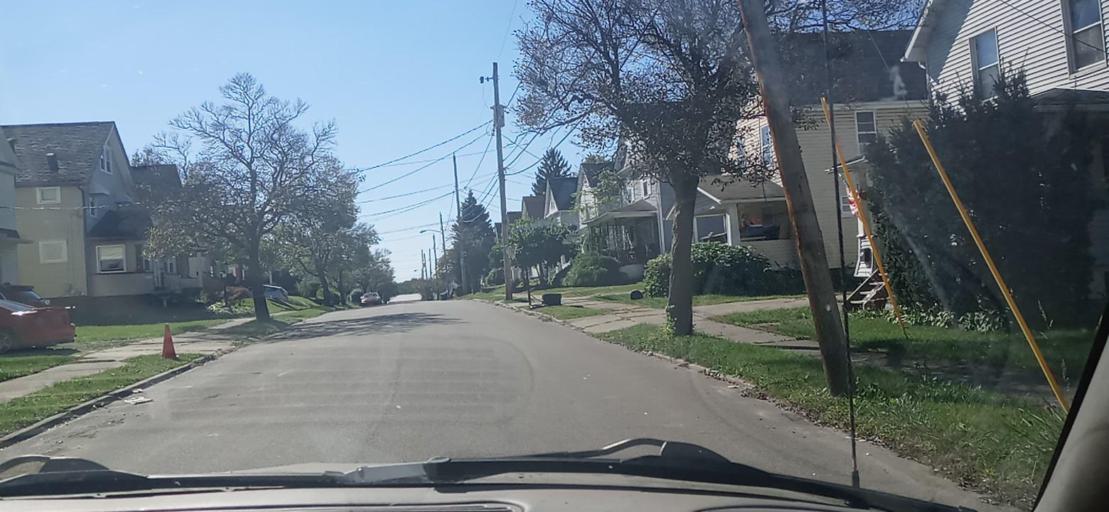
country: US
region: Ohio
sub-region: Summit County
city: Portage Lakes
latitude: 41.0416
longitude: -81.5554
